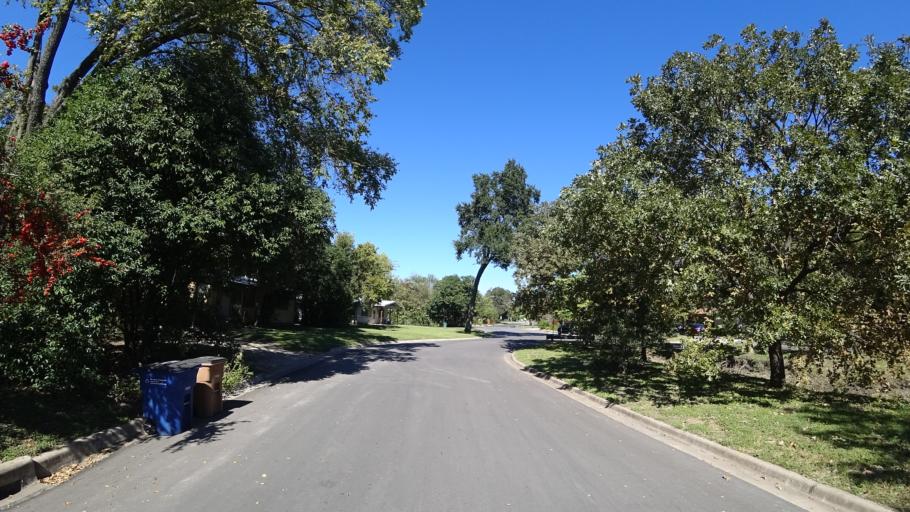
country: US
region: Texas
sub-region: Travis County
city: Austin
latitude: 30.3379
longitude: -97.7341
